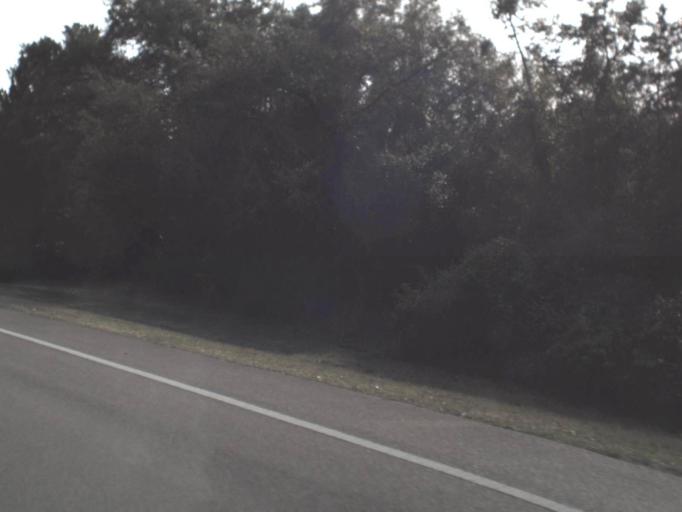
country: US
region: Florida
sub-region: Bay County
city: Tyndall Air Force Base
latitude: 30.0961
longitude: -85.6124
